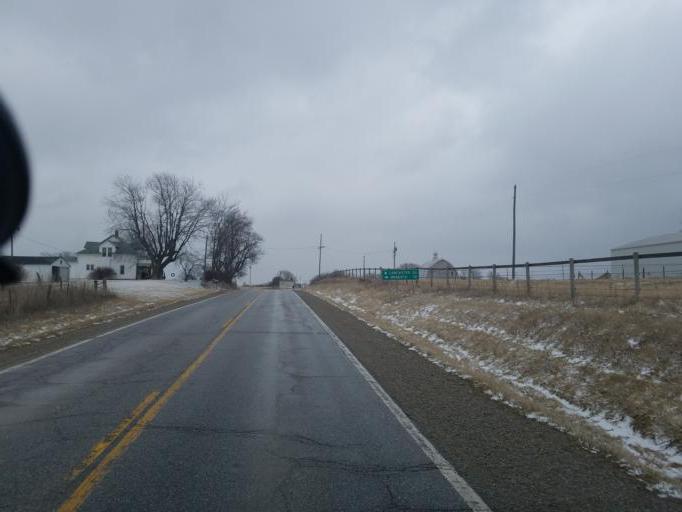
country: US
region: Missouri
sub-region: Putnam County
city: Unionville
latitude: 40.4758
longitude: -92.9781
